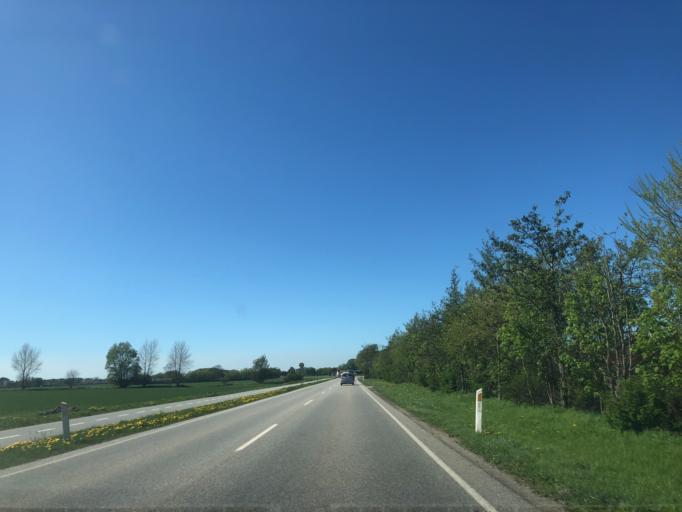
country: DK
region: Zealand
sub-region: Stevns Kommune
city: Store Heddinge
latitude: 55.3380
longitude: 12.3468
